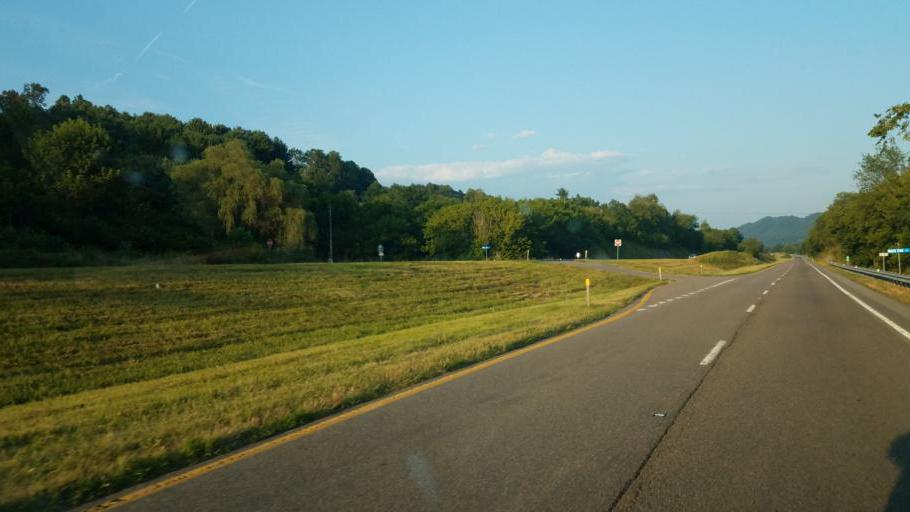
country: US
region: Virginia
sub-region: Scott County
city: Gate City
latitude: 36.6348
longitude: -82.6339
